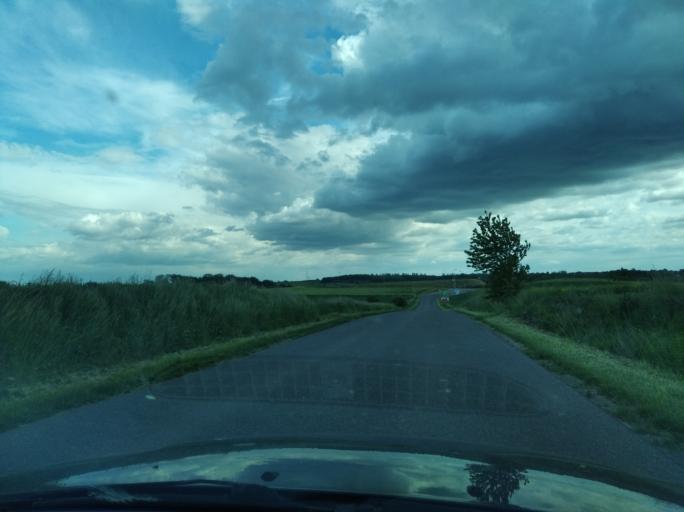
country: PL
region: Subcarpathian Voivodeship
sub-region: Powiat jaroslawski
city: Pawlosiow
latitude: 49.9501
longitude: 22.6666
